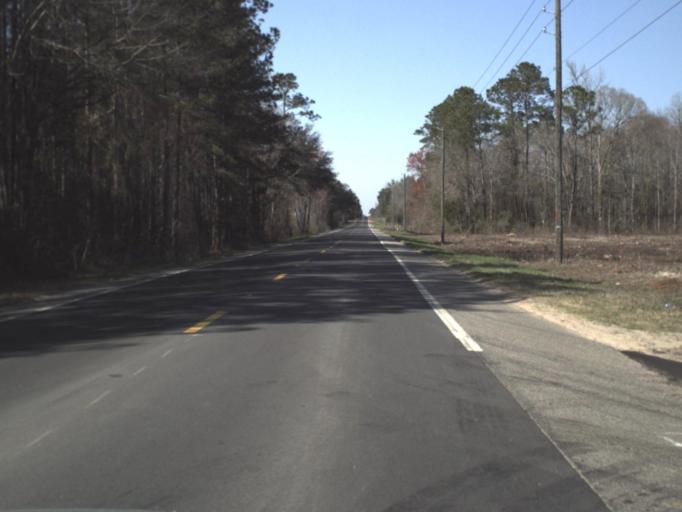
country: US
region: Florida
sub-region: Jackson County
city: Marianna
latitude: 30.6724
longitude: -85.1700
